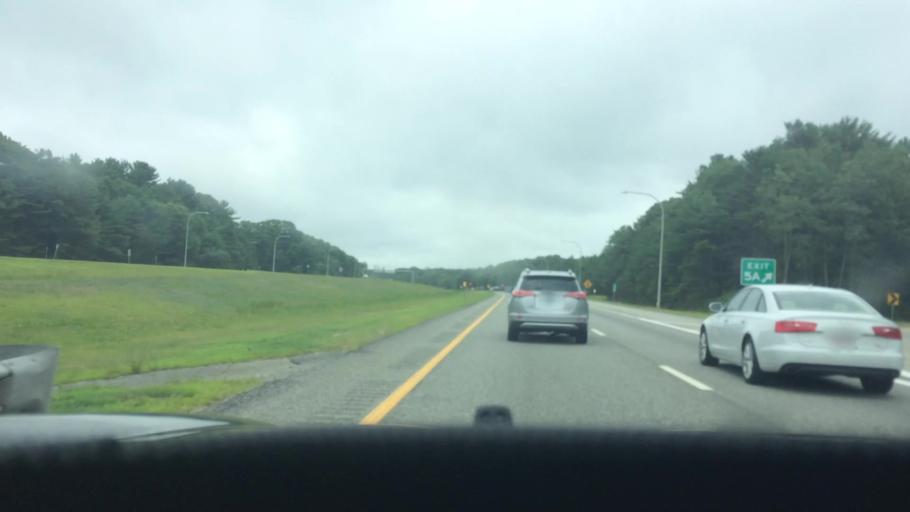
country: US
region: Rhode Island
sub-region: Kent County
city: West Greenwich
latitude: 41.6029
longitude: -71.6579
